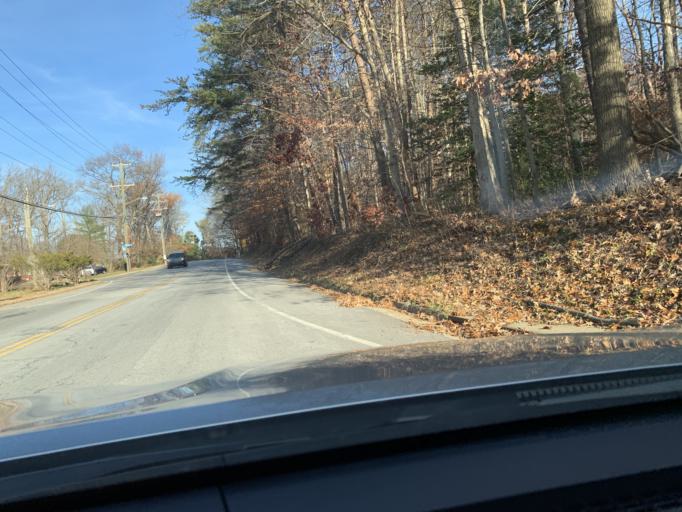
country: US
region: Virginia
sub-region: Fairfax County
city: Lake Barcroft
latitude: 38.8503
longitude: -77.1720
